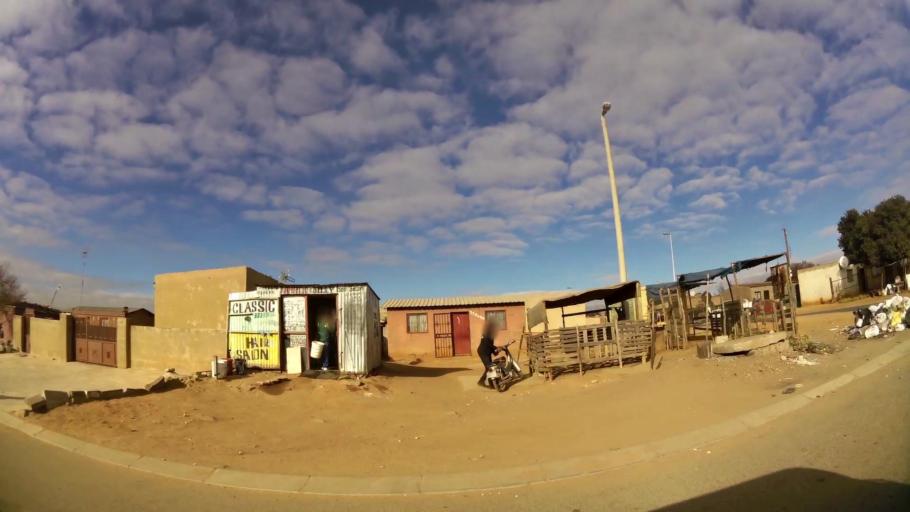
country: ZA
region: Gauteng
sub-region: City of Johannesburg Metropolitan Municipality
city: Modderfontein
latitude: -26.0450
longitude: 28.1853
